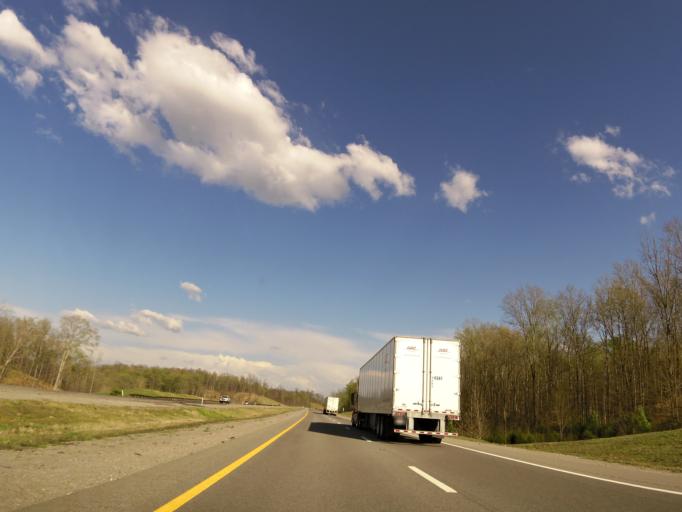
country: US
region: Tennessee
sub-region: Williamson County
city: Thompson's Station
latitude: 35.8244
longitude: -87.0499
